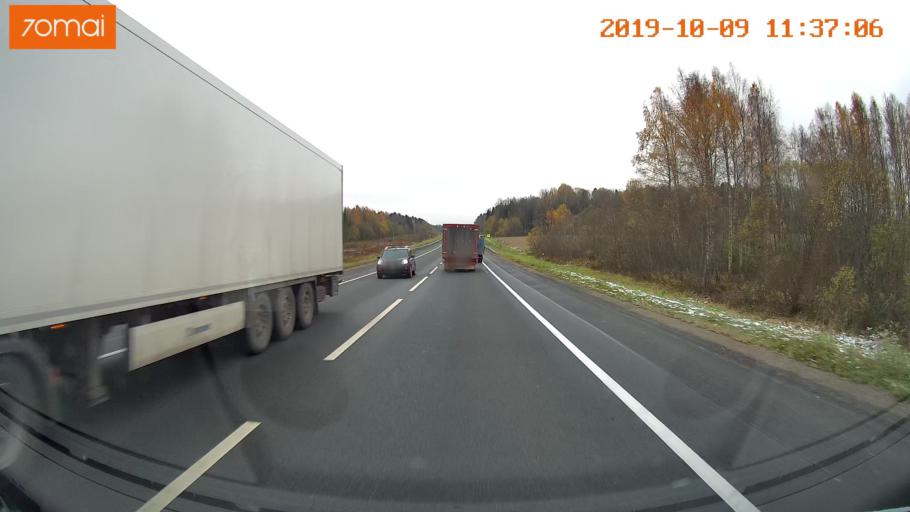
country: RU
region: Vologda
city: Gryazovets
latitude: 58.9827
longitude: 40.1428
